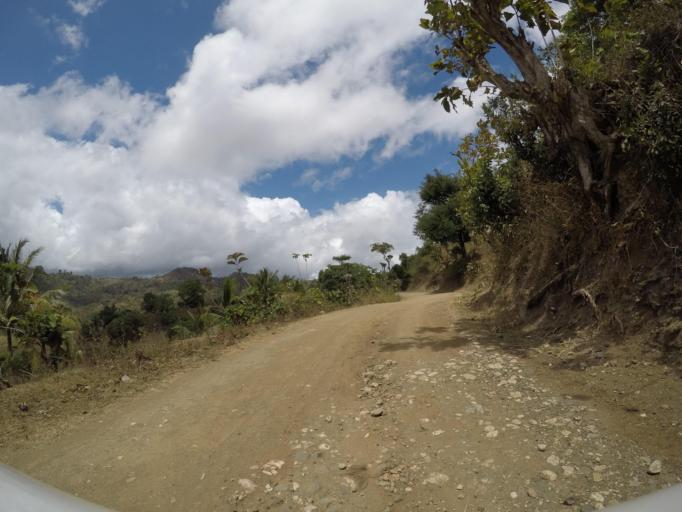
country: TL
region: Lautem
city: Lospalos
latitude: -8.5421
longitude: 126.8370
